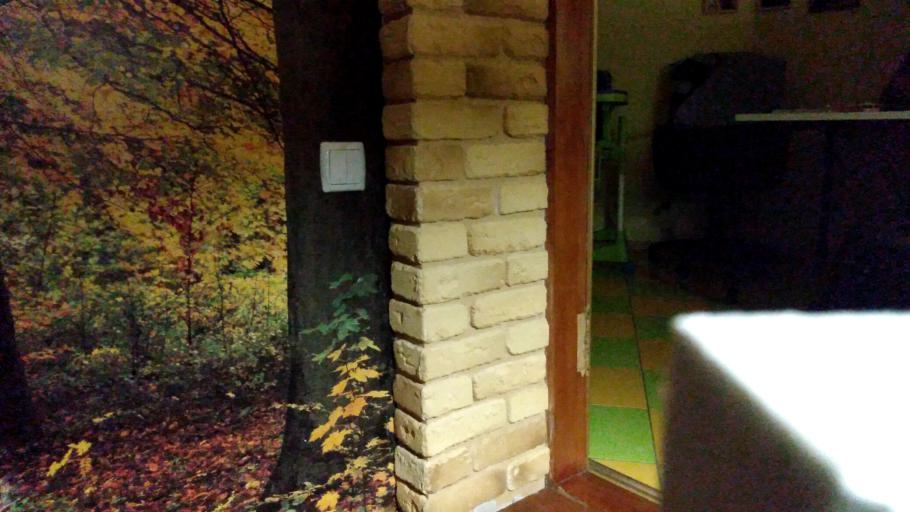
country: RU
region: Vologda
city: Lipin Bor
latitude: 60.7698
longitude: 38.0441
